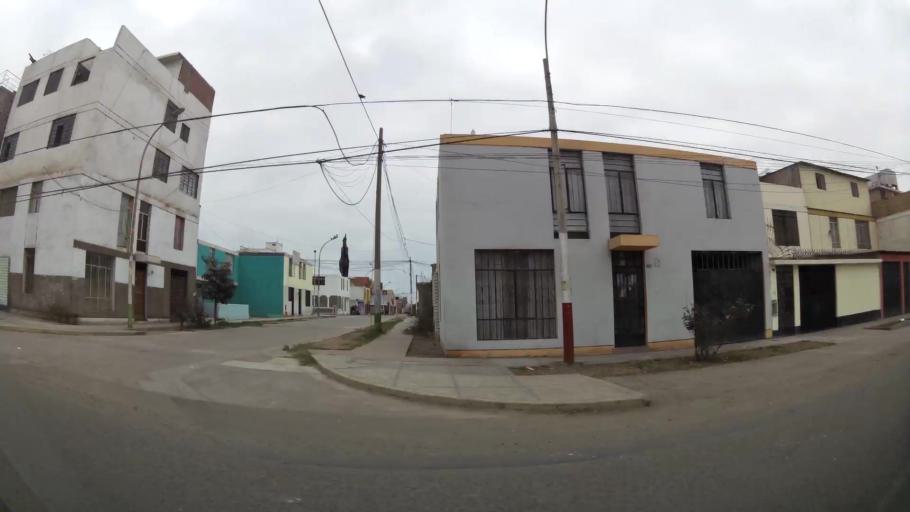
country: PE
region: Callao
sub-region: Callao
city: Callao
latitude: -12.0533
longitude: -77.1080
